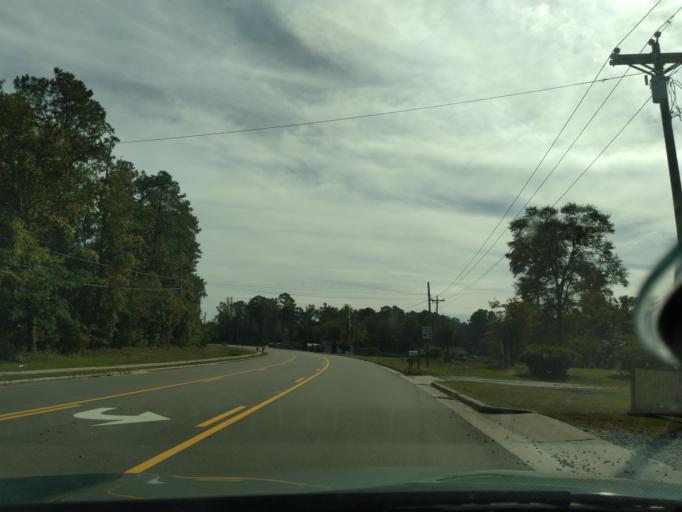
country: US
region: North Carolina
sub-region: Beaufort County
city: River Road
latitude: 35.5170
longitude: -77.0047
